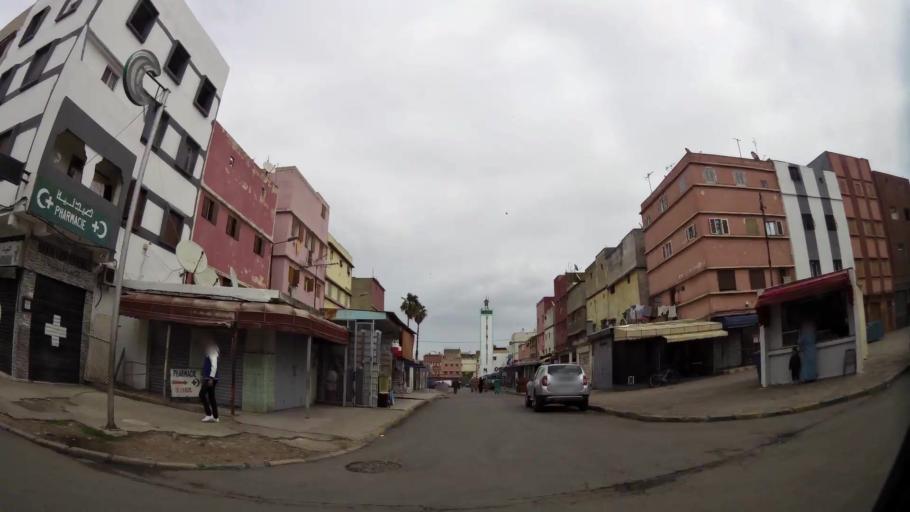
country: MA
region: Grand Casablanca
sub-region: Mediouna
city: Tit Mellil
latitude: 33.6121
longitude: -7.5072
